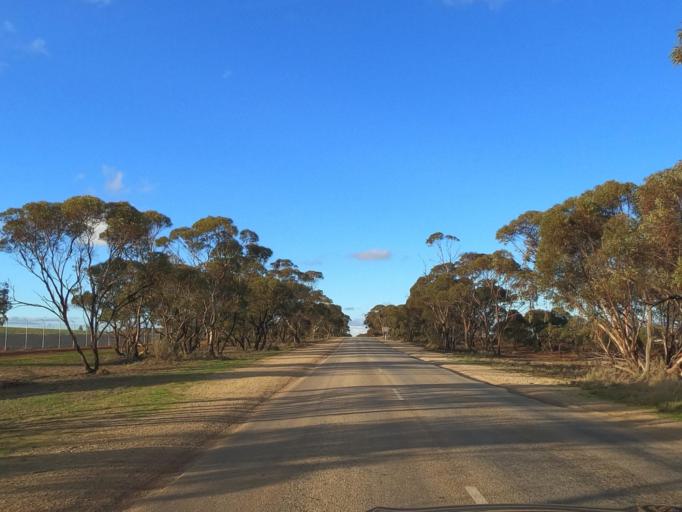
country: AU
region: Victoria
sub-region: Swan Hill
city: Swan Hill
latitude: -35.3499
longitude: 143.5111
